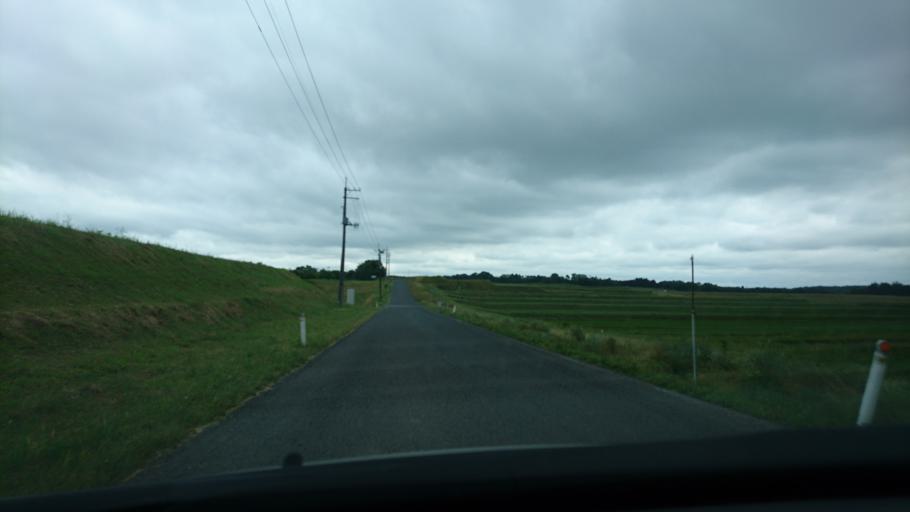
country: JP
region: Iwate
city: Ichinoseki
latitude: 38.8856
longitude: 141.1948
